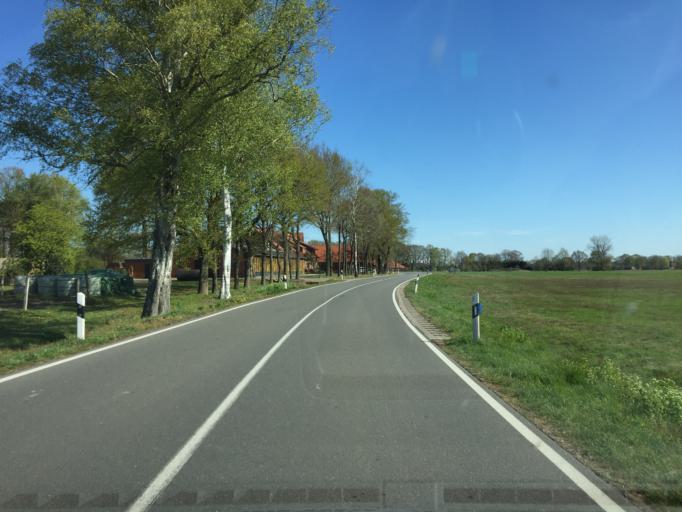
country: DE
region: Lower Saxony
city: Wehrbleck
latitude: 52.5785
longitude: 8.6971
